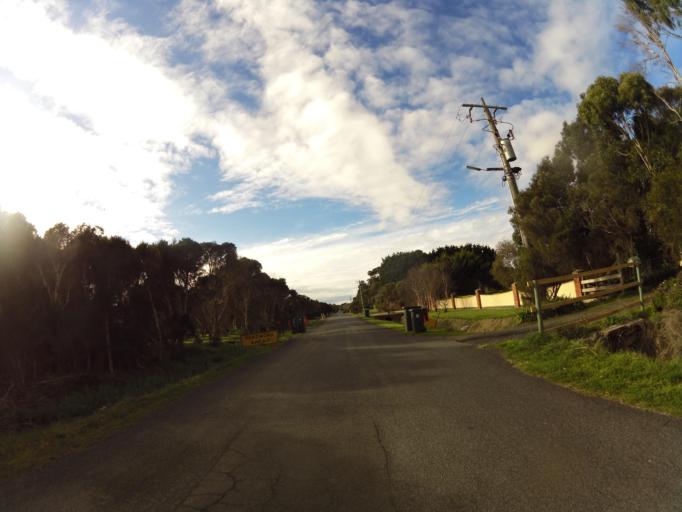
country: AU
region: Victoria
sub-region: Bass Coast
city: North Wonthaggi
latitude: -38.6166
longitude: 145.5773
